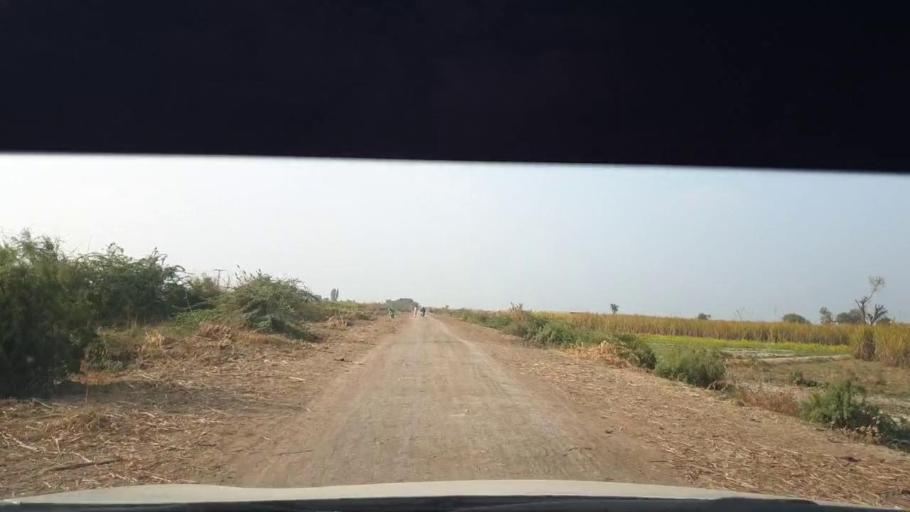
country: PK
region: Sindh
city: Berani
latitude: 25.7461
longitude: 68.9479
